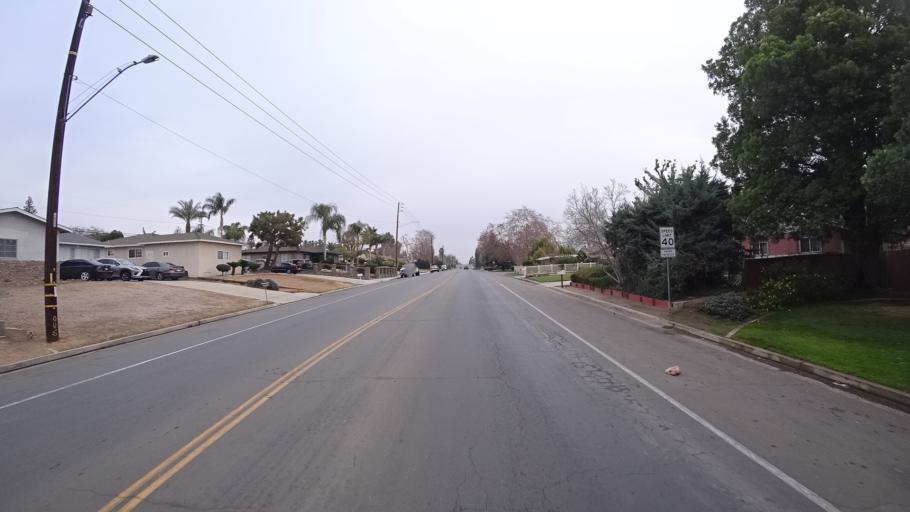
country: US
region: California
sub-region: Kern County
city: Bakersfield
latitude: 35.3832
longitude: -118.9491
